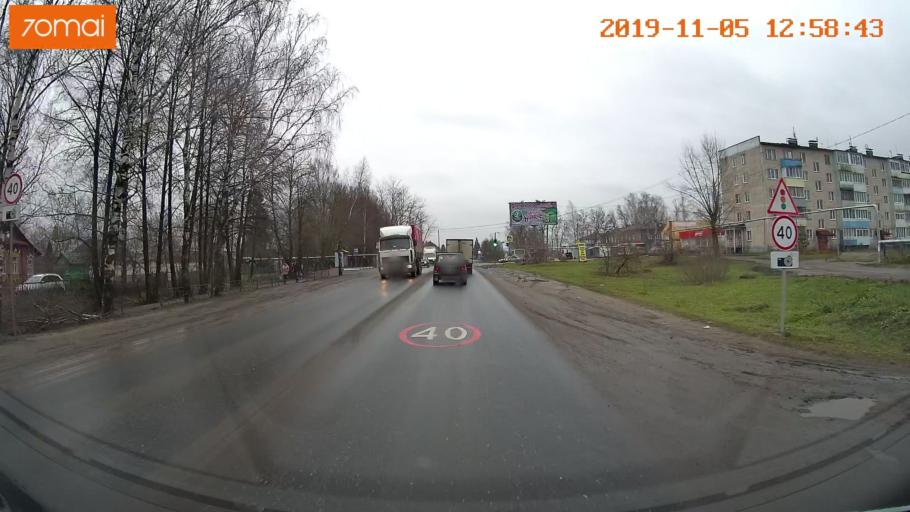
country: RU
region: Ivanovo
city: Kokhma
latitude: 56.9207
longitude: 41.1213
